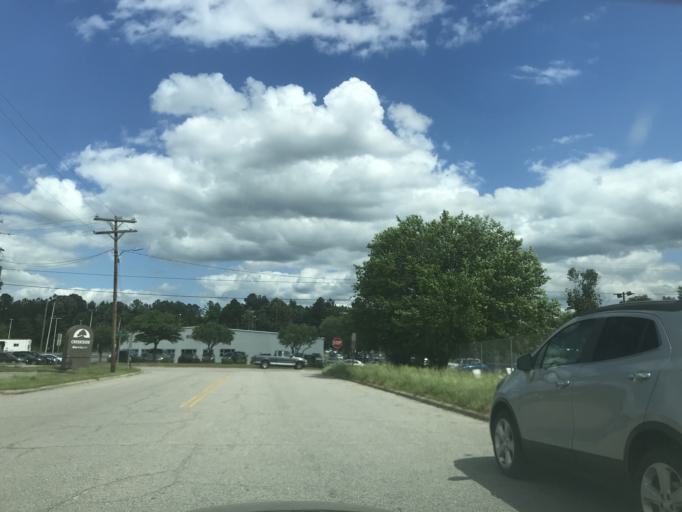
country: US
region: North Carolina
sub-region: Wake County
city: Raleigh
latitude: 35.8159
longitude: -78.6219
